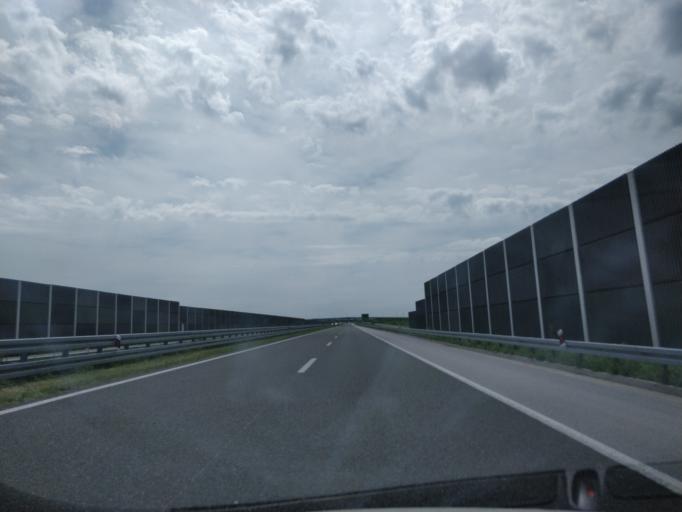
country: HR
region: Zagrebacka
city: Gradici
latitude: 45.7056
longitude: 16.0497
